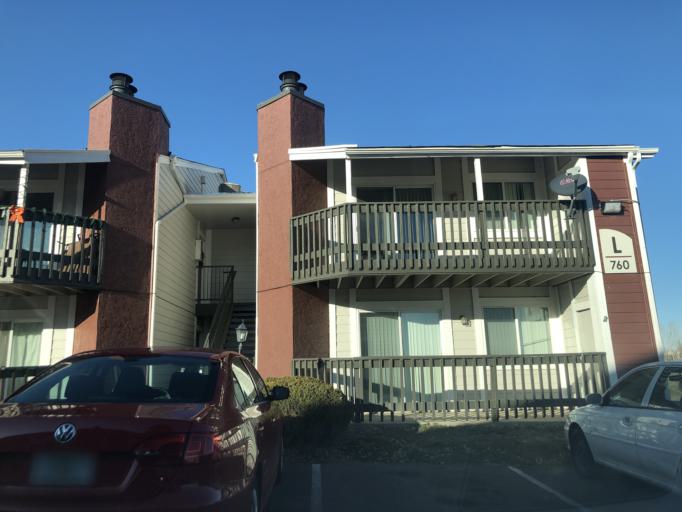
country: US
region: Colorado
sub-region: Adams County
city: Aurora
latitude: 39.7041
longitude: -104.8067
